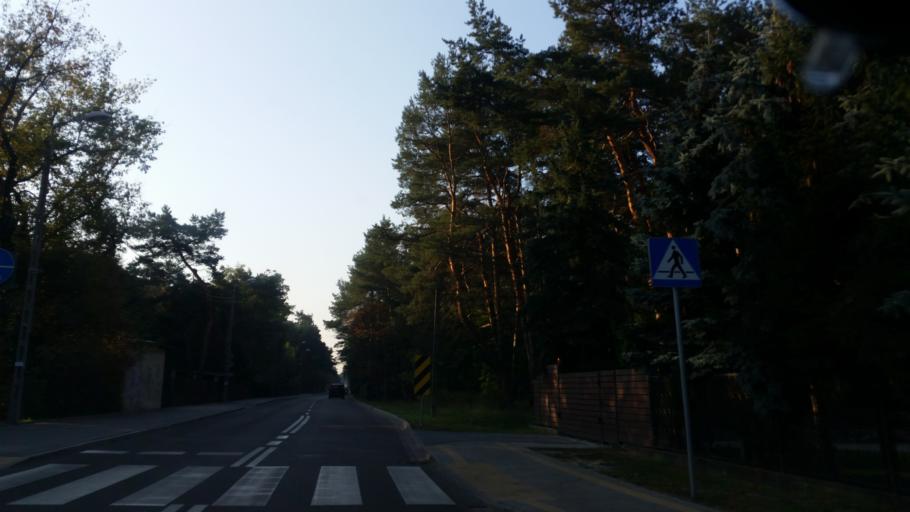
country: PL
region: Masovian Voivodeship
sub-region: Powiat otwocki
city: Jozefow
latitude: 52.1411
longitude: 21.2155
